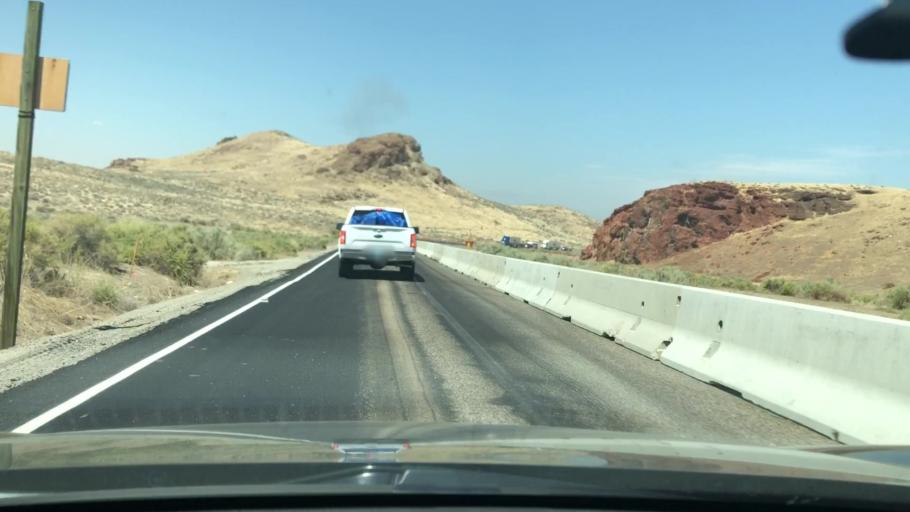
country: US
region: Idaho
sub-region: Owyhee County
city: Marsing
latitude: 43.4586
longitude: -116.8651
